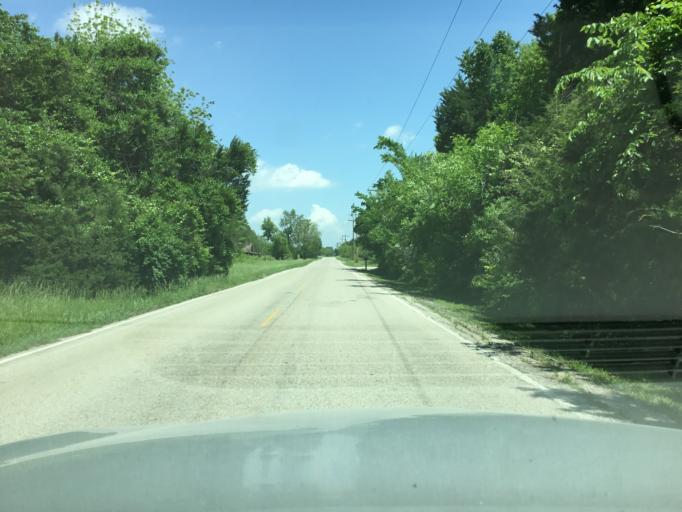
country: US
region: Kansas
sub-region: Labette County
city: Parsons
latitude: 37.3424
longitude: -95.3039
